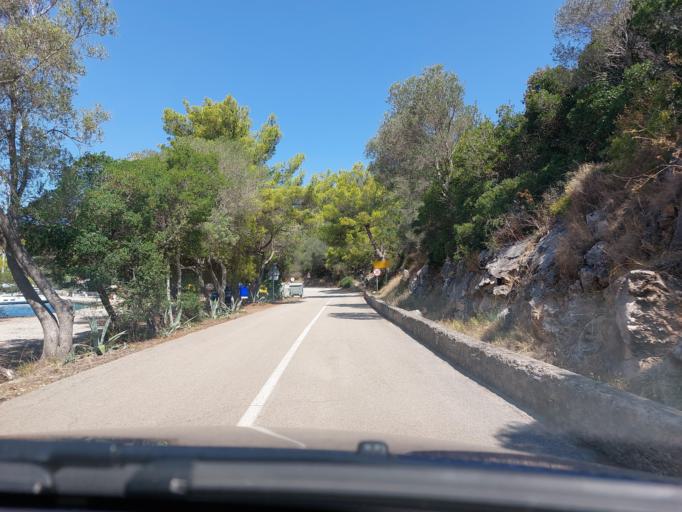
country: HR
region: Dubrovacko-Neretvanska
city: Smokvica
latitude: 42.7640
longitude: 16.8235
